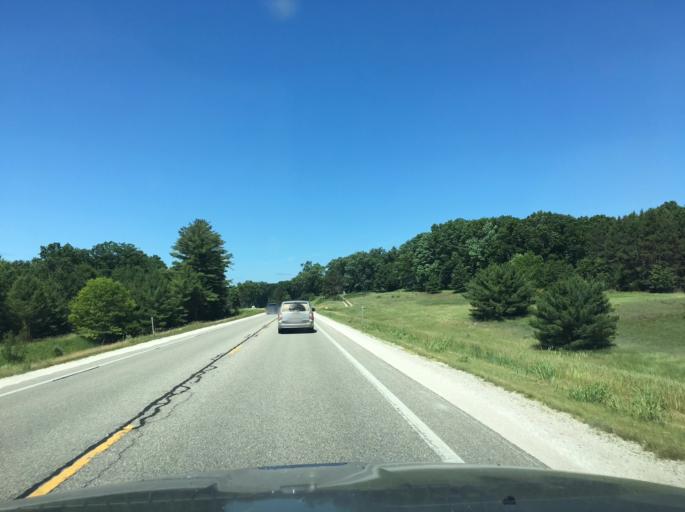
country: US
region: Michigan
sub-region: Osceola County
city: Reed City
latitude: 43.8910
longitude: -85.6522
